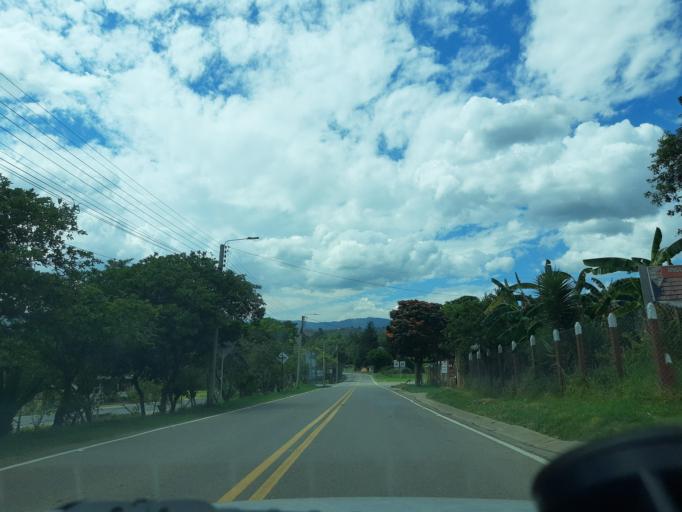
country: CO
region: Boyaca
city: Raquira
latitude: 5.5719
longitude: -73.6524
